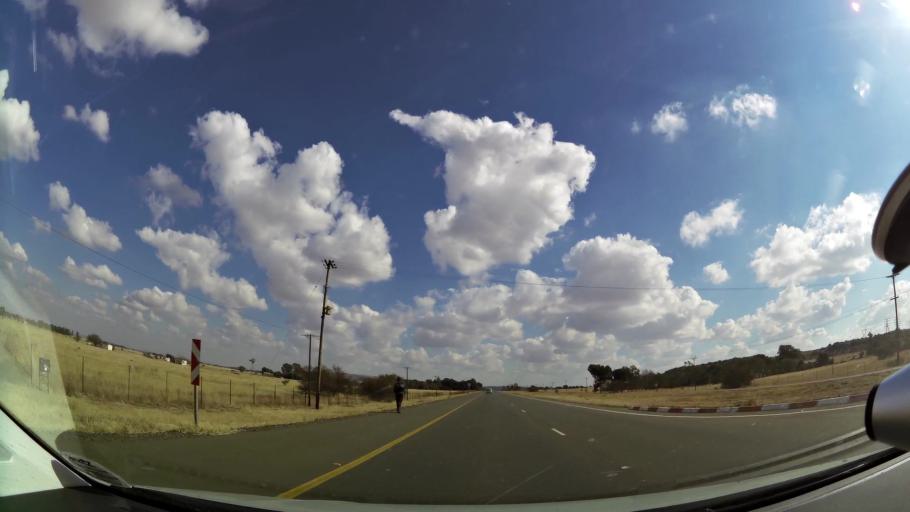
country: ZA
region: Orange Free State
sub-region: Mangaung Metropolitan Municipality
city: Bloemfontein
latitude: -29.1374
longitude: 26.1213
